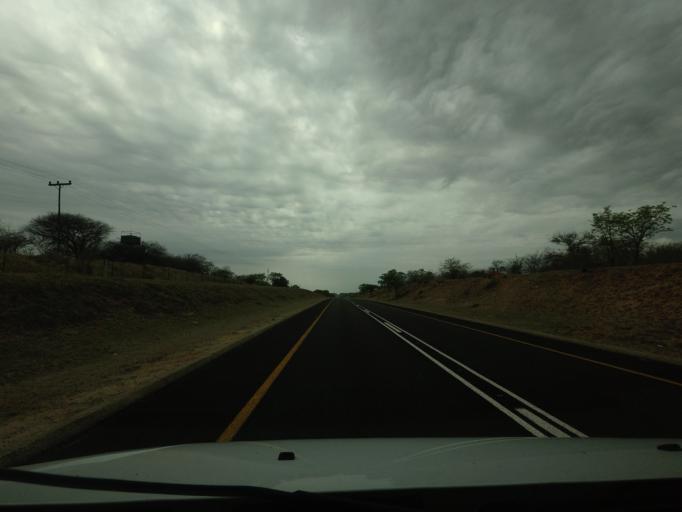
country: ZA
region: Limpopo
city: Thulamahashi
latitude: -24.5642
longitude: 31.1290
